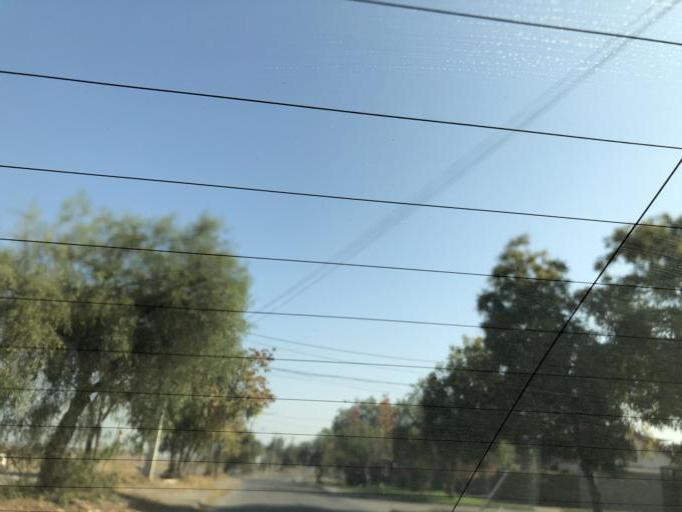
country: CL
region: Santiago Metropolitan
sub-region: Provincia de Cordillera
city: Puente Alto
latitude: -33.6169
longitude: -70.5580
